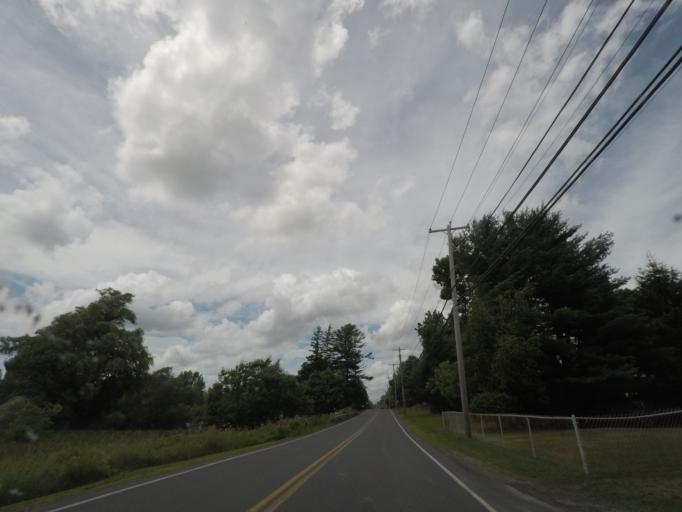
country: US
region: New York
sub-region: Rensselaer County
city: Wynantskill
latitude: 42.7060
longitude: -73.6198
